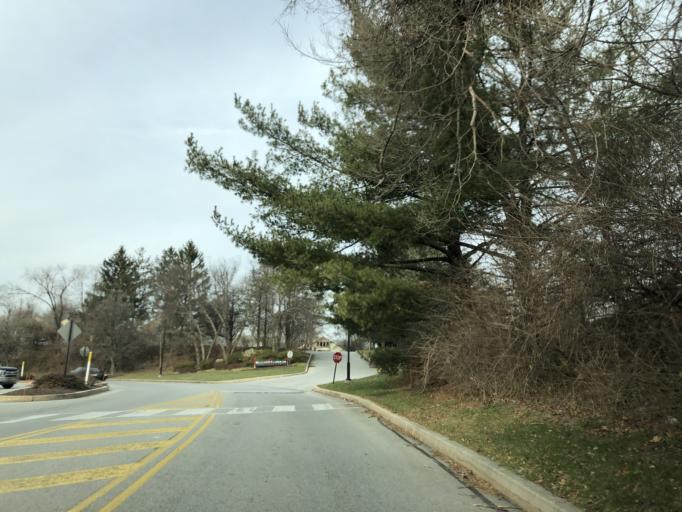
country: US
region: Pennsylvania
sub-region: Chester County
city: Exton
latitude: 40.0329
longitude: -75.6220
